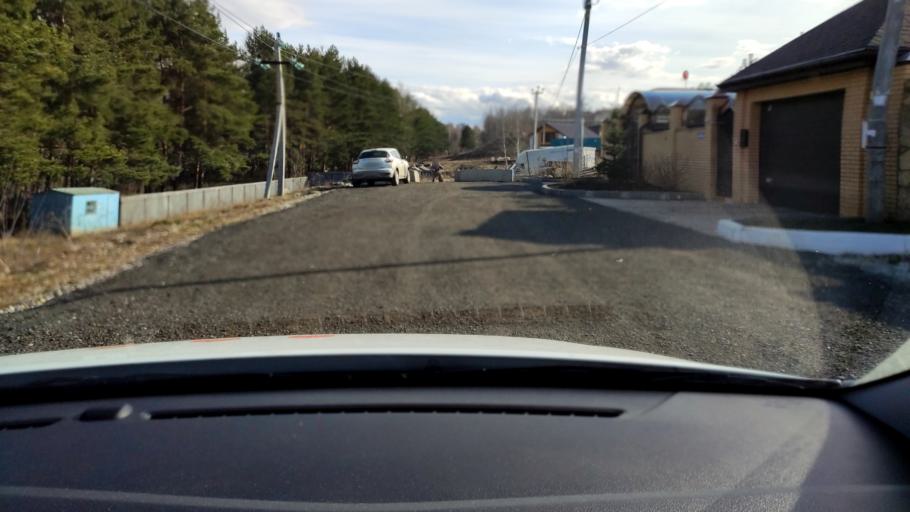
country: RU
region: Tatarstan
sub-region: Gorod Kazan'
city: Kazan
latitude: 55.7802
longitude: 49.2478
